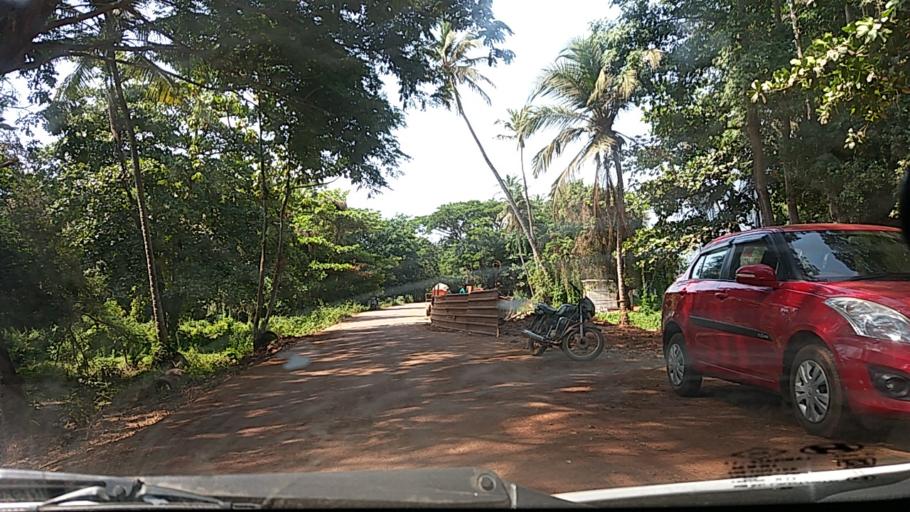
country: IN
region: Goa
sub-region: South Goa
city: Madgaon
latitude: 15.2770
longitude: 73.9528
